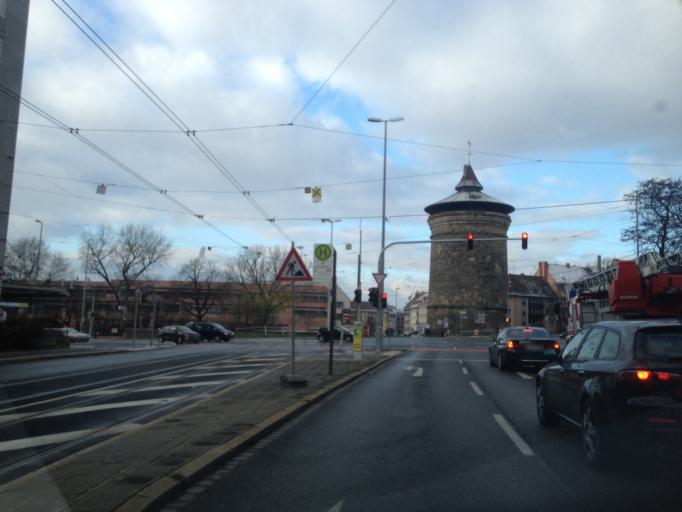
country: DE
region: Bavaria
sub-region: Regierungsbezirk Mittelfranken
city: Nuernberg
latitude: 49.4577
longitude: 11.0902
